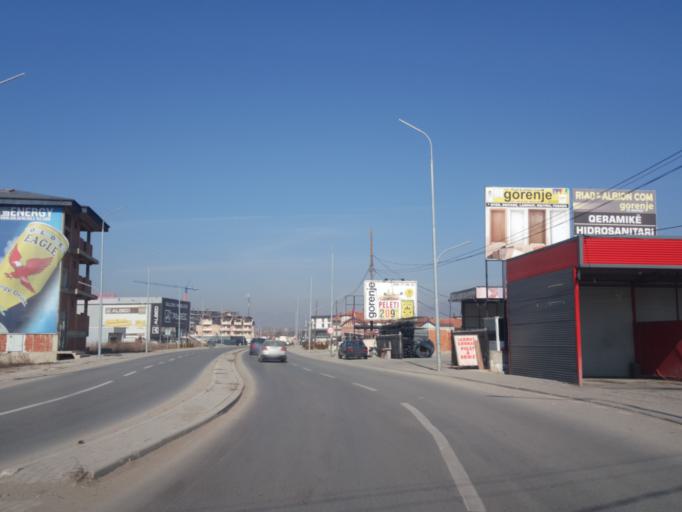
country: XK
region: Mitrovica
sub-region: Vushtrri
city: Vushtrri
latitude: 42.8153
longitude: 20.9831
